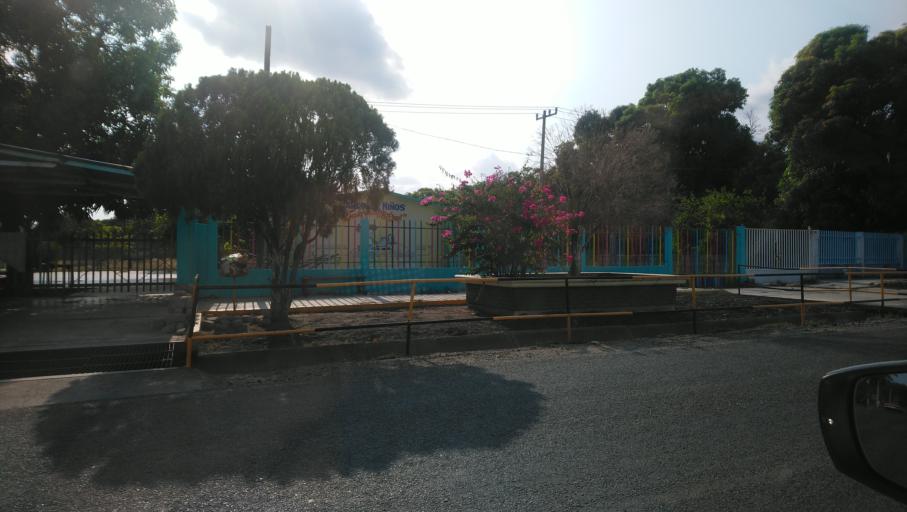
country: MX
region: Oaxaca
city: San Jeronimo Ixtepec
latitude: 16.5870
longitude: -95.1639
